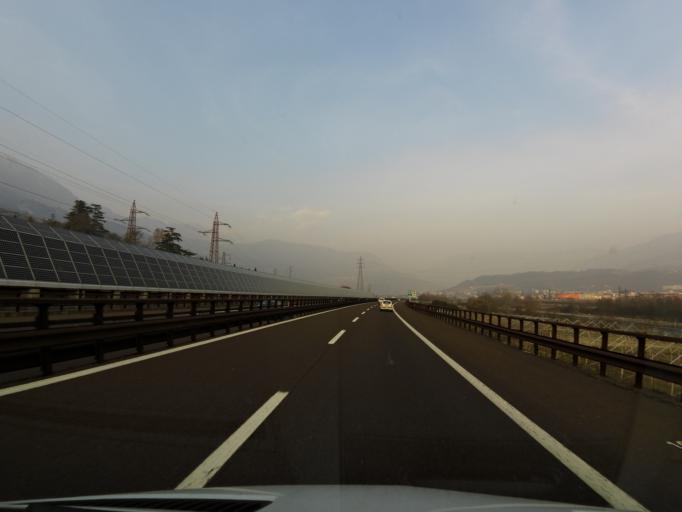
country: IT
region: Trentino-Alto Adige
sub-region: Provincia di Trento
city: Isera
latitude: 45.8930
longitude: 11.0161
